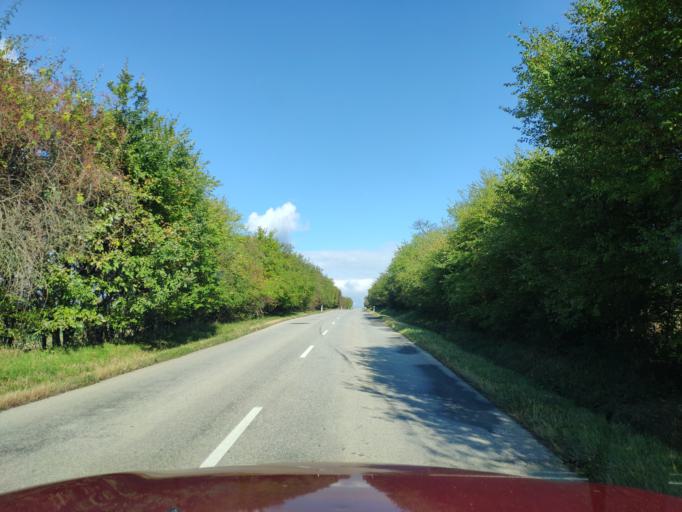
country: SK
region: Presovsky
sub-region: Okres Presov
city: Presov
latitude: 48.8912
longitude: 21.2603
